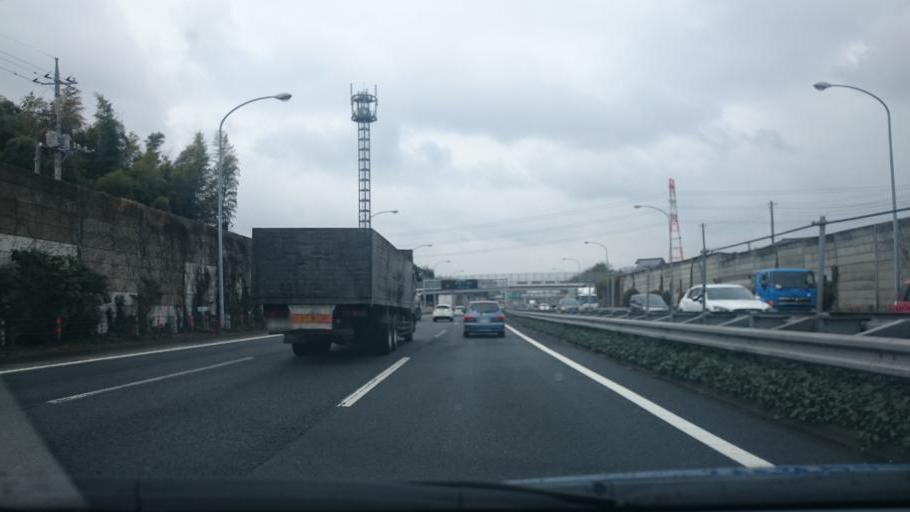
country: JP
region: Saitama
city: Sakado
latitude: 35.9195
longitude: 139.4172
